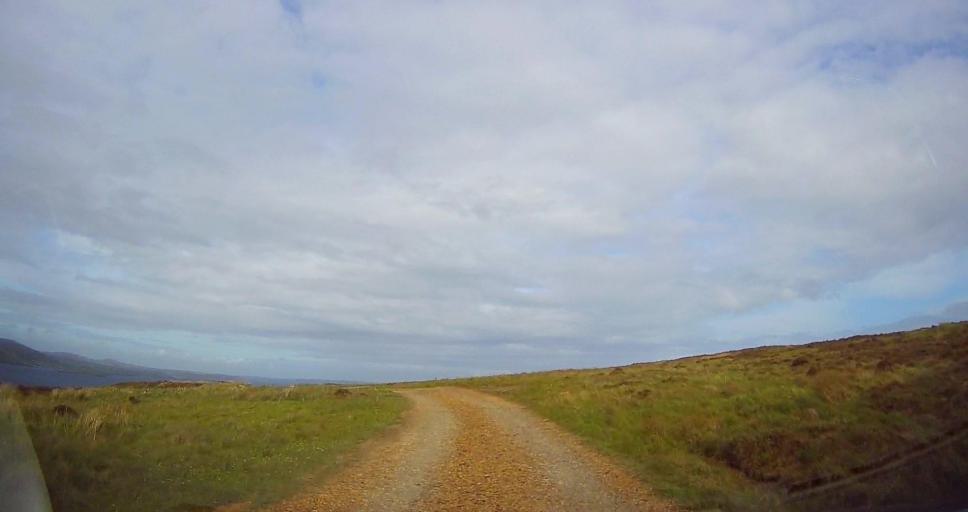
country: GB
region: Scotland
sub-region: Orkney Islands
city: Stromness
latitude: 58.8795
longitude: -3.2444
